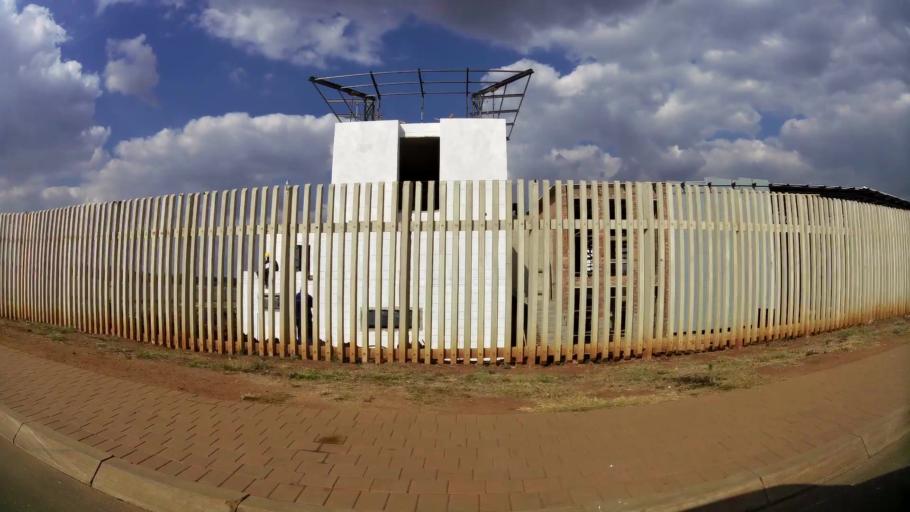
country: ZA
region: Gauteng
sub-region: Ekurhuleni Metropolitan Municipality
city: Tembisa
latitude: -25.9325
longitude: 28.2090
